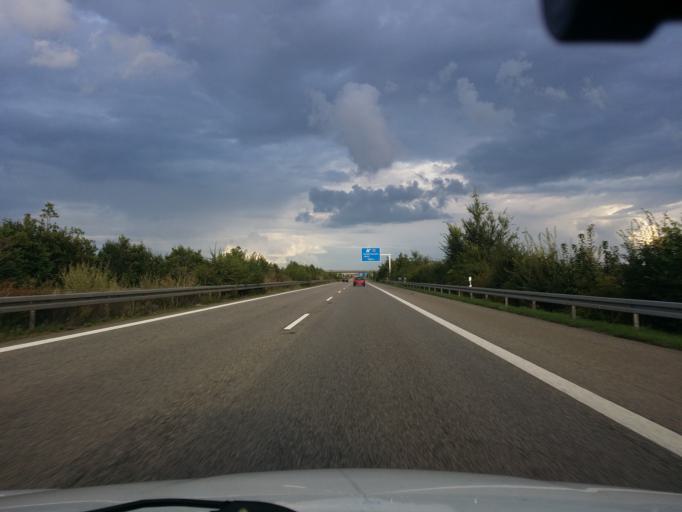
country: DE
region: Saxony-Anhalt
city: Wallhausen
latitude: 51.4504
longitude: 11.2424
